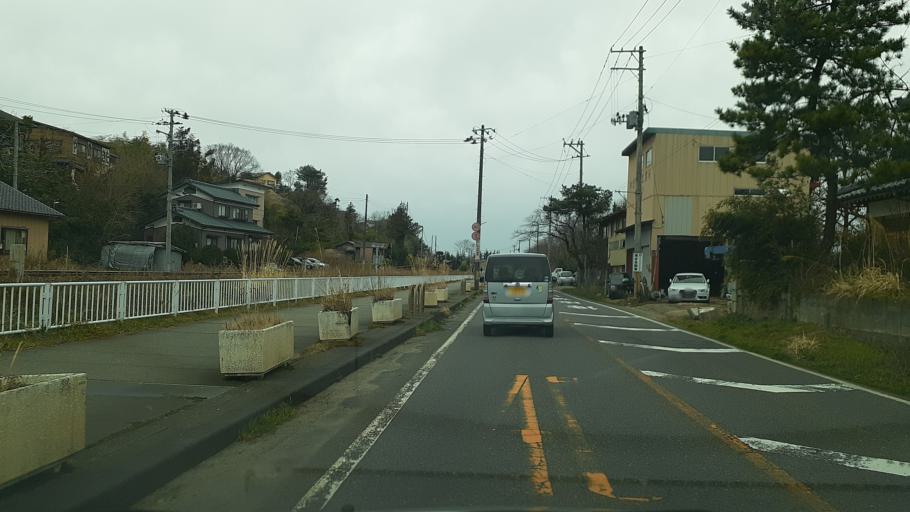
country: JP
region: Niigata
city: Niitsu-honcho
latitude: 37.7909
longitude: 139.1386
